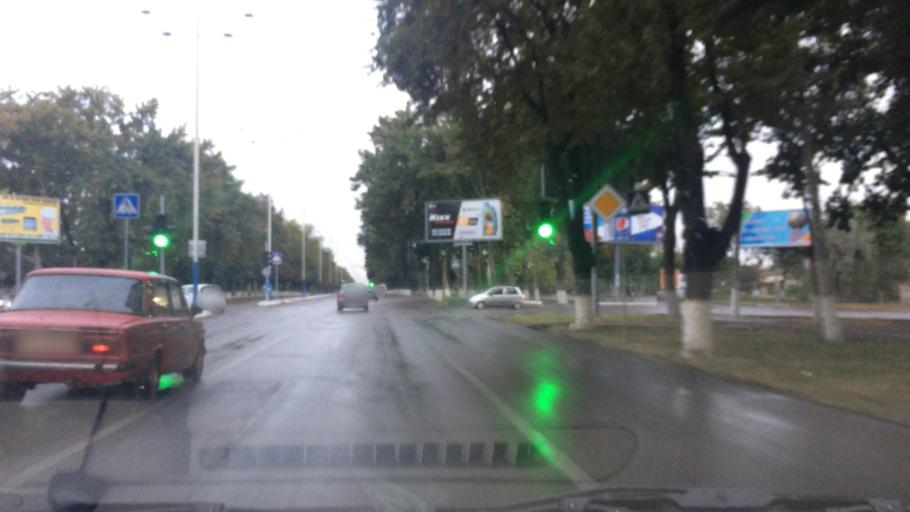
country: UZ
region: Toshkent Shahri
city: Tashkent
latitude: 41.2685
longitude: 69.2010
